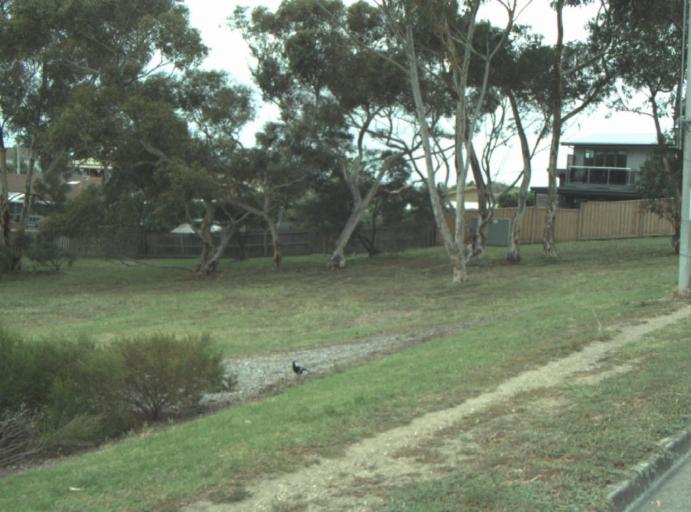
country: AU
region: Victoria
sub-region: Greater Geelong
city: Wandana Heights
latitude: -38.1742
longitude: 144.3067
